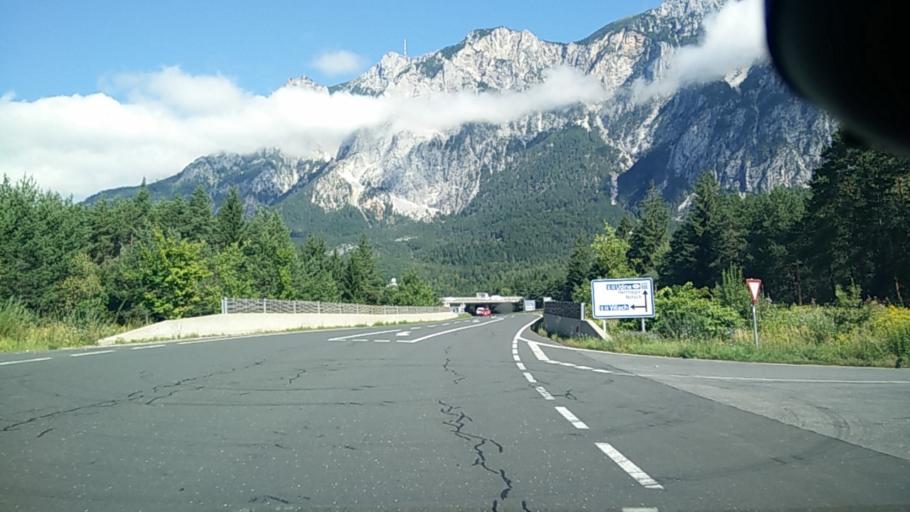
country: AT
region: Carinthia
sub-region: Politischer Bezirk Villach Land
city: Arnoldstein
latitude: 46.5664
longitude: 13.6949
